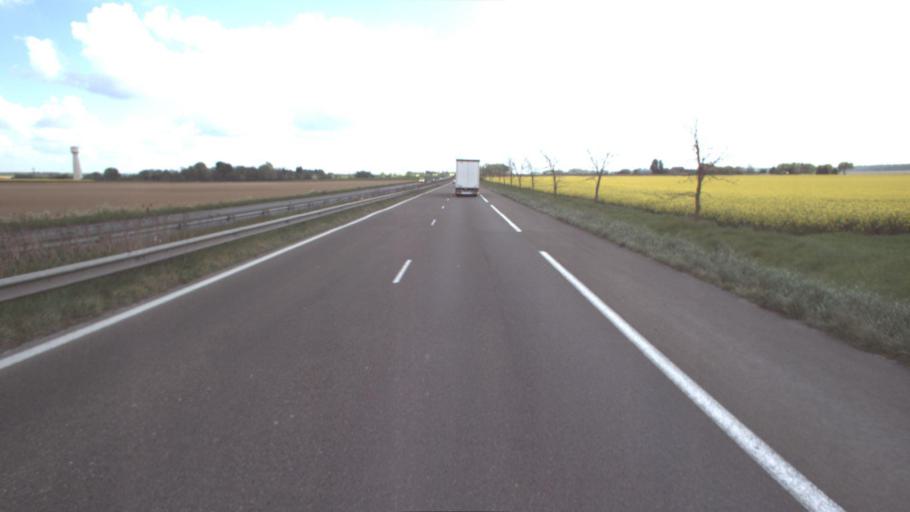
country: FR
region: Ile-de-France
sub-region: Departement de Seine-et-Marne
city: Rozay-en-Brie
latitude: 48.6863
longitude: 2.9852
